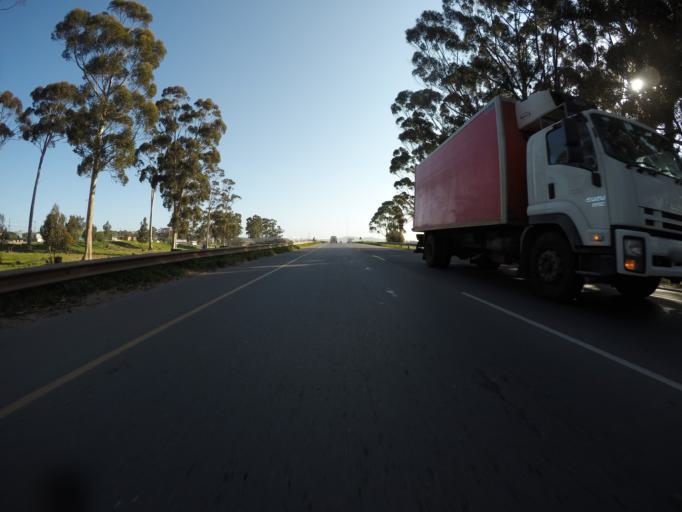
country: ZA
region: Western Cape
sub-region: City of Cape Town
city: Kraaifontein
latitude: -33.7813
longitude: 18.7149
